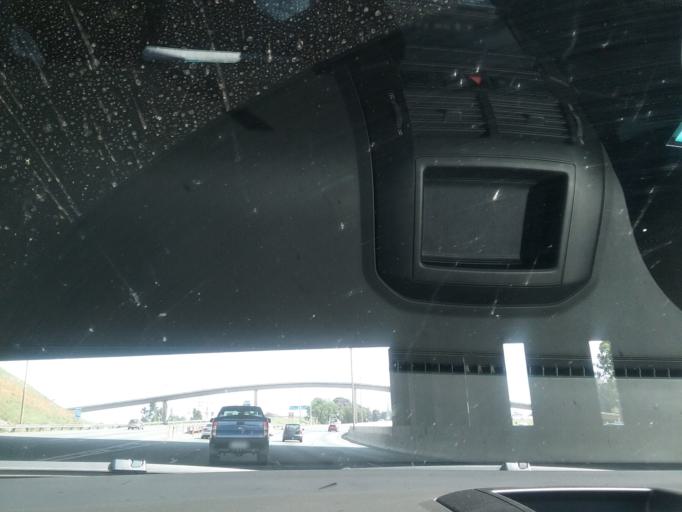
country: ZA
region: Gauteng
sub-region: Ekurhuleni Metropolitan Municipality
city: Germiston
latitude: -26.2075
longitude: 28.1367
